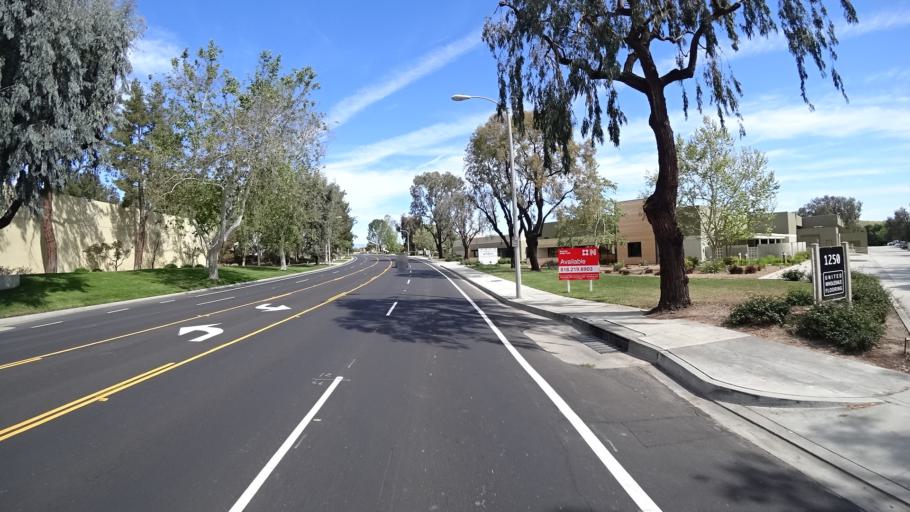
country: US
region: California
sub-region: Ventura County
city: Casa Conejo
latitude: 34.1955
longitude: -118.9217
